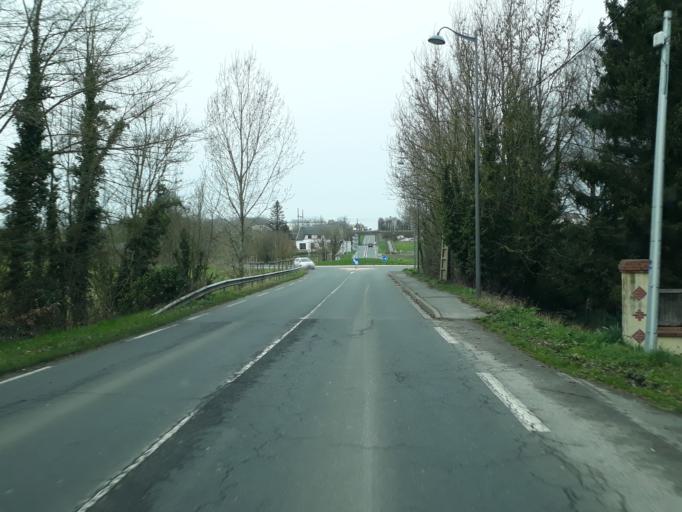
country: FR
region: Haute-Normandie
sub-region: Departement de la Seine-Maritime
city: Beuzeville-la-Grenier
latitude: 49.6004
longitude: 0.4176
